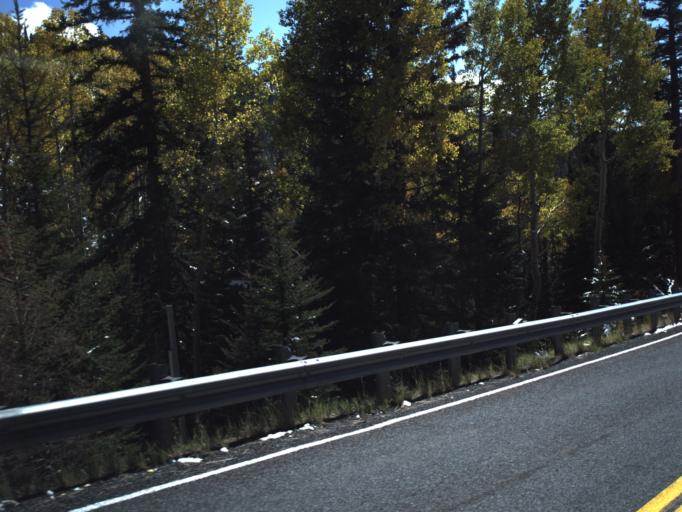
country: US
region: Utah
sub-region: Piute County
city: Junction
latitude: 38.3201
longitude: -112.3869
